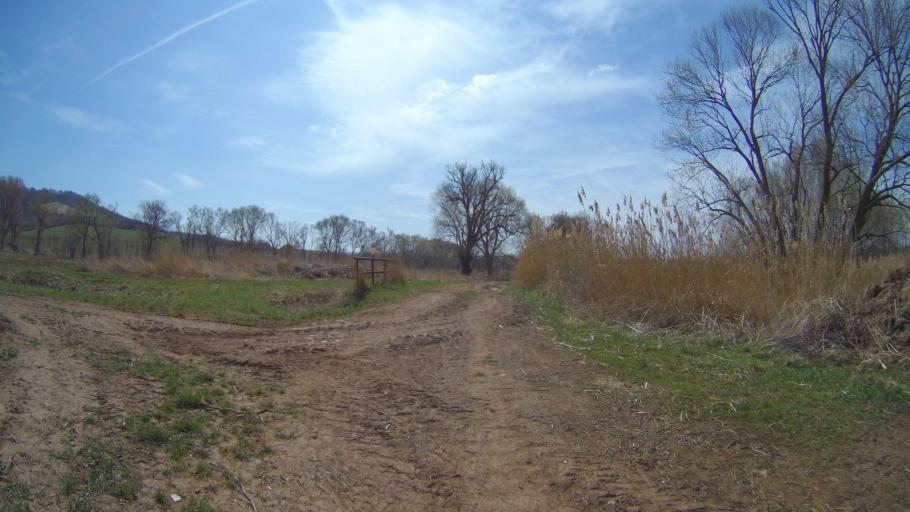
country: CZ
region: Ustecky
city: Kryry
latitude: 50.2051
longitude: 13.4626
